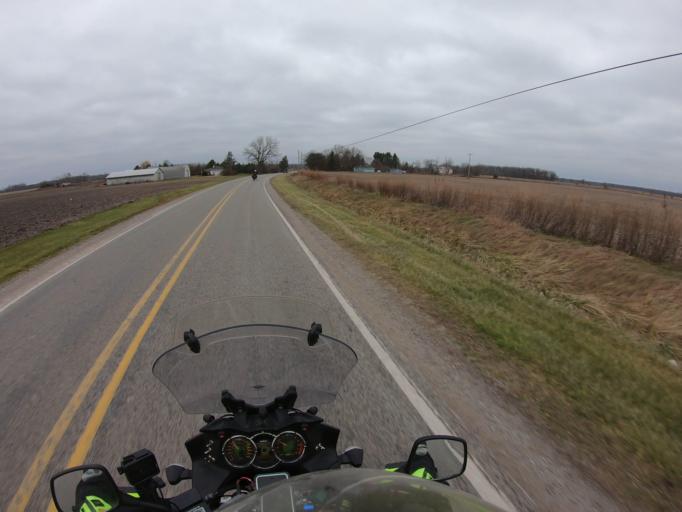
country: US
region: Michigan
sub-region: Saginaw County
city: Saint Charles
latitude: 43.2684
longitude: -84.1156
